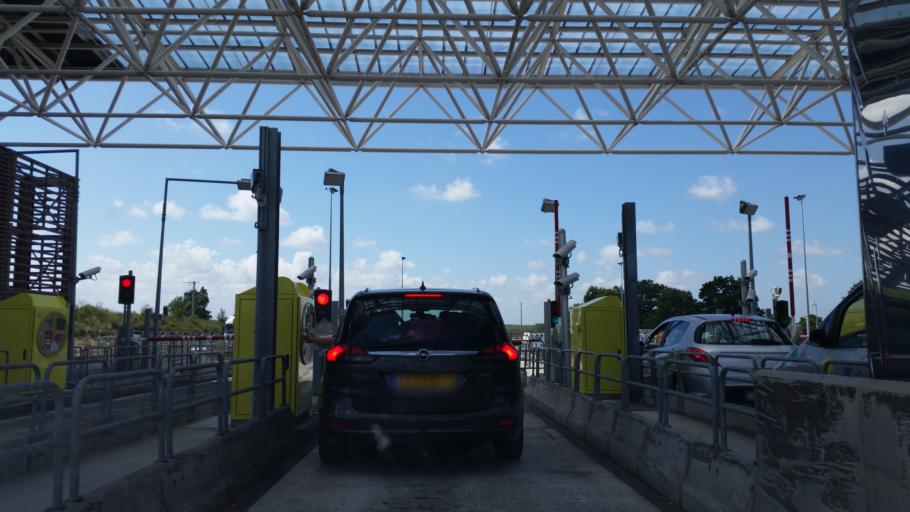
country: FR
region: Lower Normandy
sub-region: Departement du Calvados
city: Dozule
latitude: 49.2309
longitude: -0.0710
